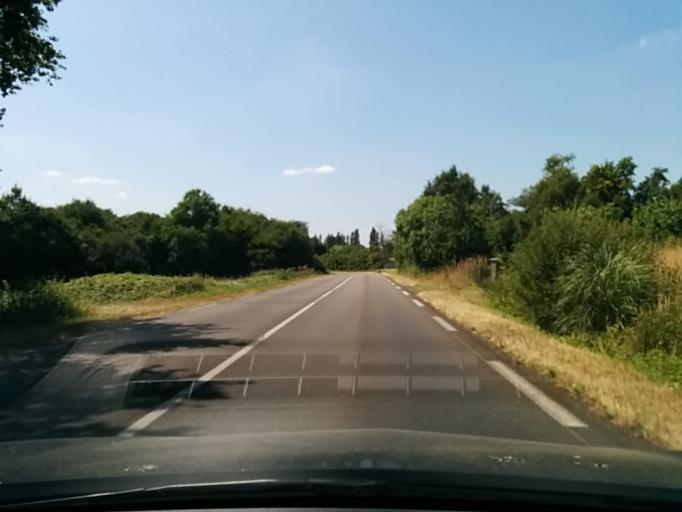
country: FR
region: Midi-Pyrenees
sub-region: Departement du Gers
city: Nogaro
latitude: 43.7488
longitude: -0.0650
